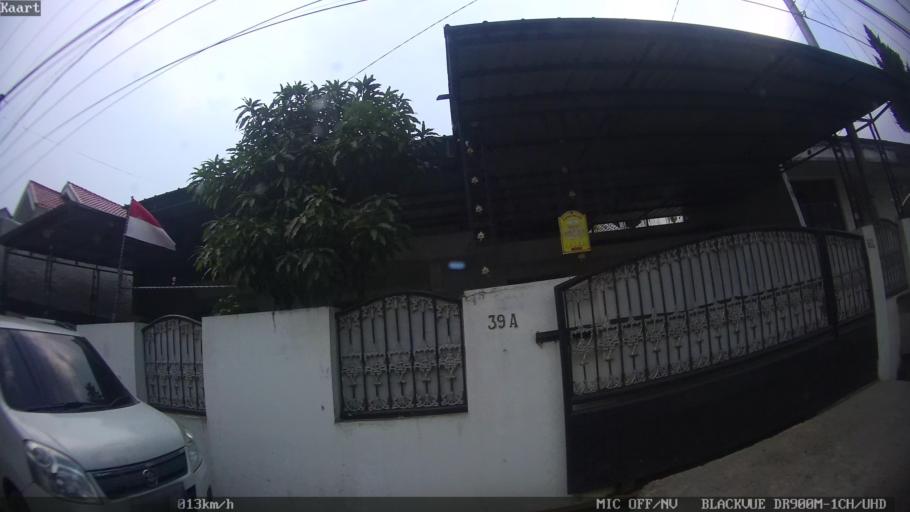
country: ID
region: Lampung
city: Bandarlampung
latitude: -5.4216
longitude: 105.2770
